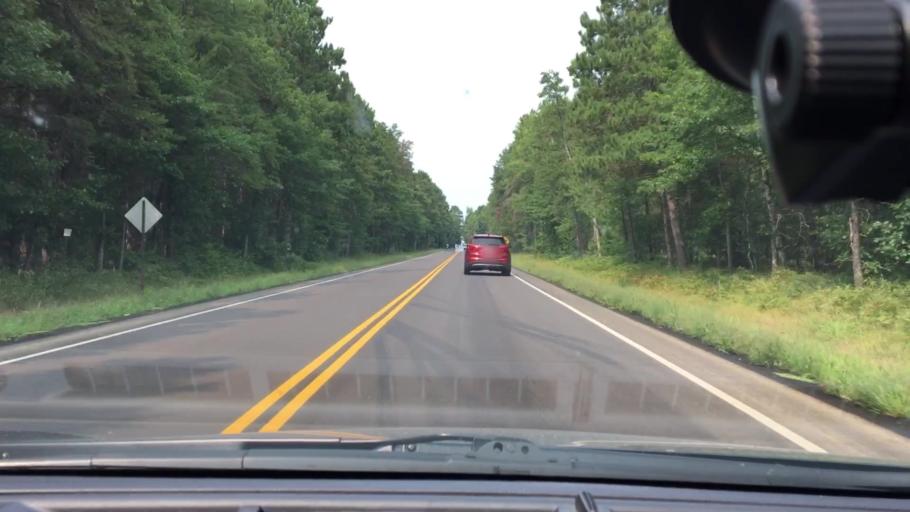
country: US
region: Minnesota
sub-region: Crow Wing County
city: Breezy Point
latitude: 46.5306
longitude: -94.1823
